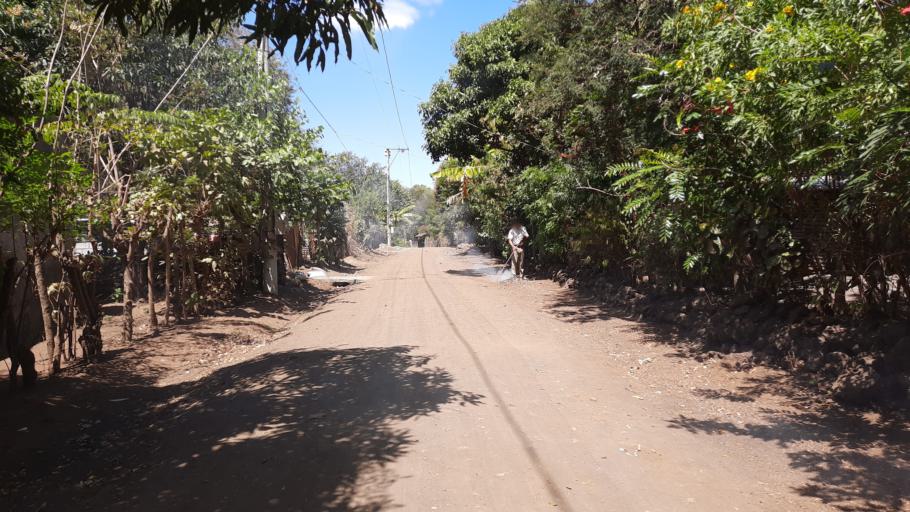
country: NI
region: Masaya
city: Ticuantepe
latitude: 12.0299
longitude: -86.1669
